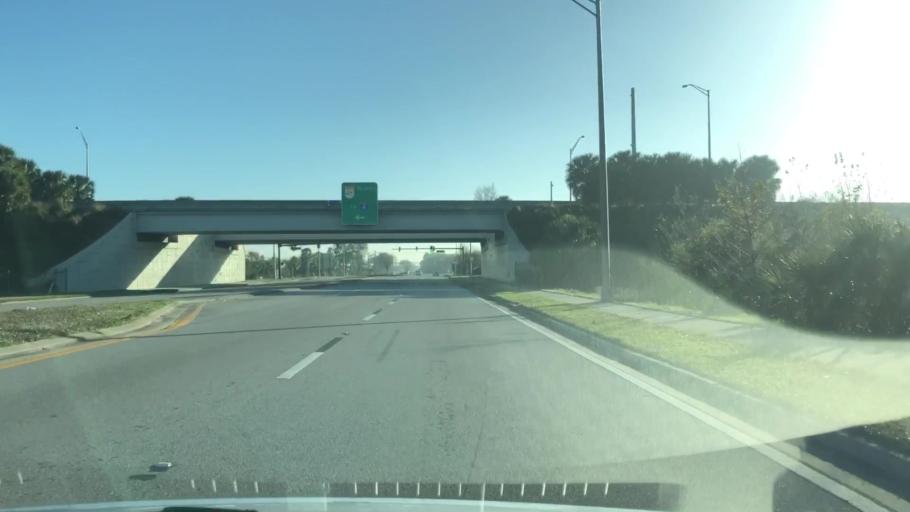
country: US
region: Florida
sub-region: Seminole County
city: Lake Mary
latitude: 28.7864
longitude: -81.3024
